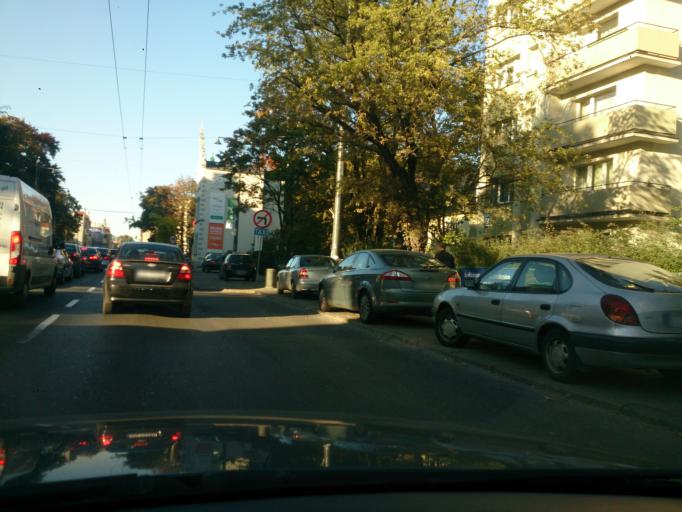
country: PL
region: Pomeranian Voivodeship
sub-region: Sopot
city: Sopot
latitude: 54.4394
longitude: 18.5606
